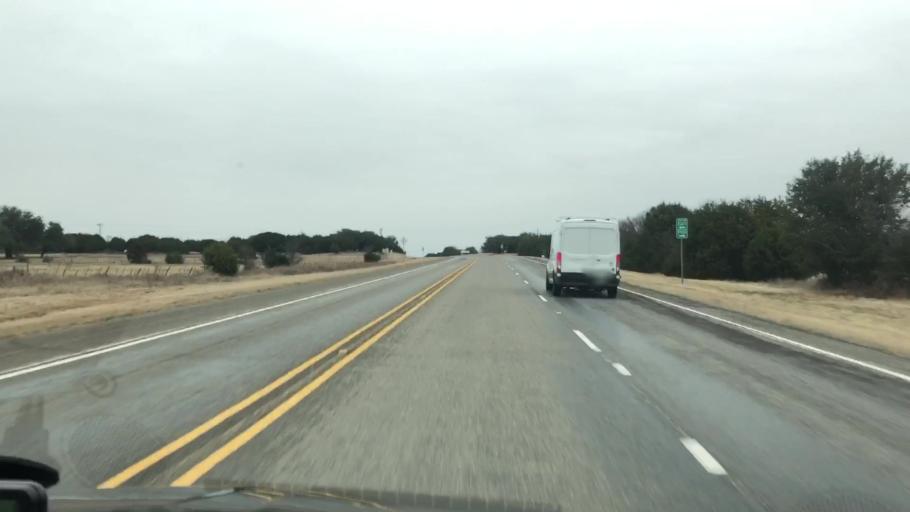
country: US
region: Texas
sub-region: Lampasas County
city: Lampasas
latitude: 31.1661
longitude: -98.1756
